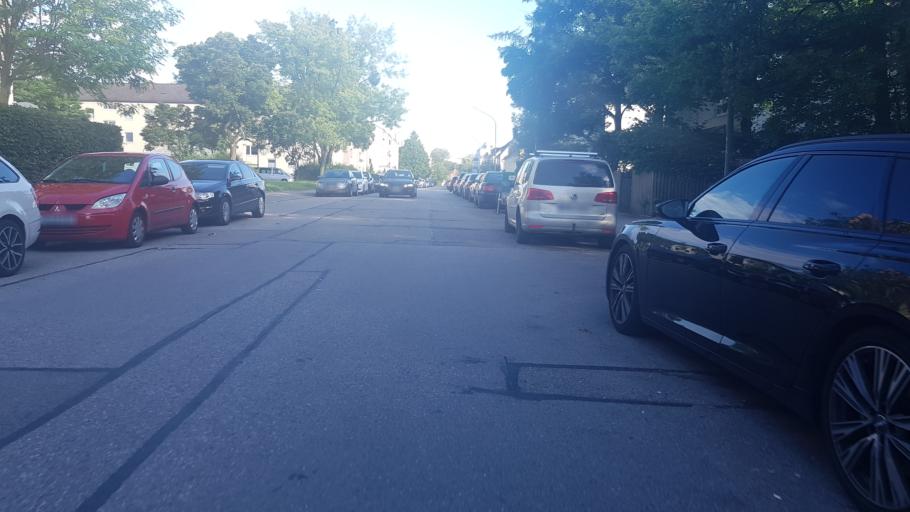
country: DE
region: Bavaria
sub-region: Upper Bavaria
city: Pasing
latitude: 48.1502
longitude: 11.4492
